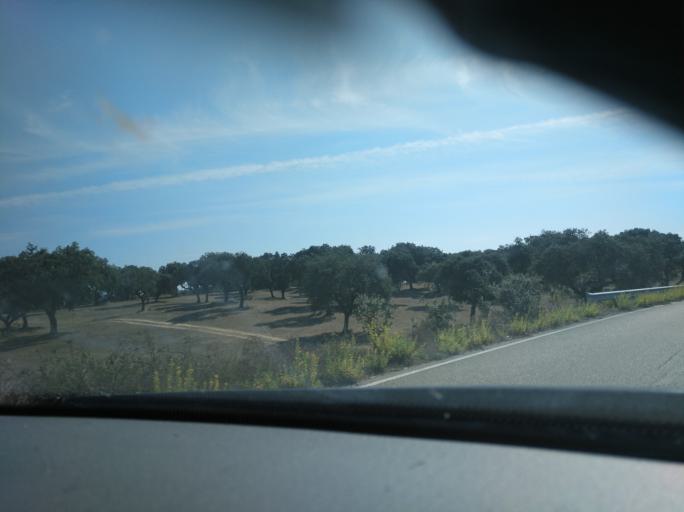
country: PT
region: Evora
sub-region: Arraiolos
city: Arraiolos
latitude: 38.6903
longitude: -8.0881
